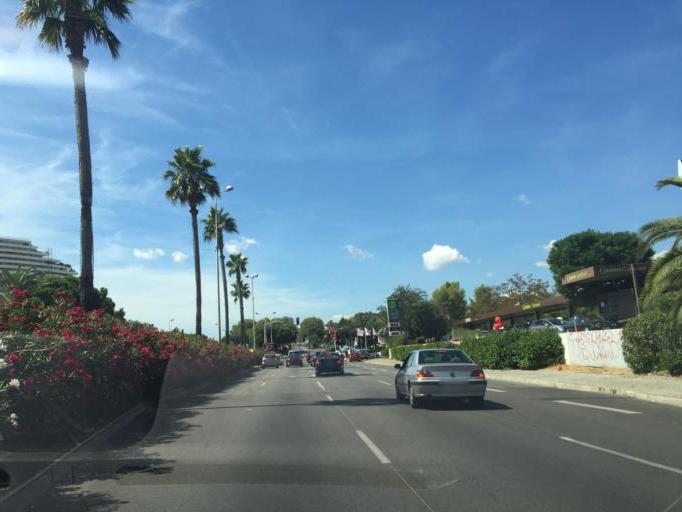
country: FR
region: Provence-Alpes-Cote d'Azur
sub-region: Departement des Alpes-Maritimes
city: Cagnes-sur-Mer
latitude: 43.6401
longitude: 7.1395
